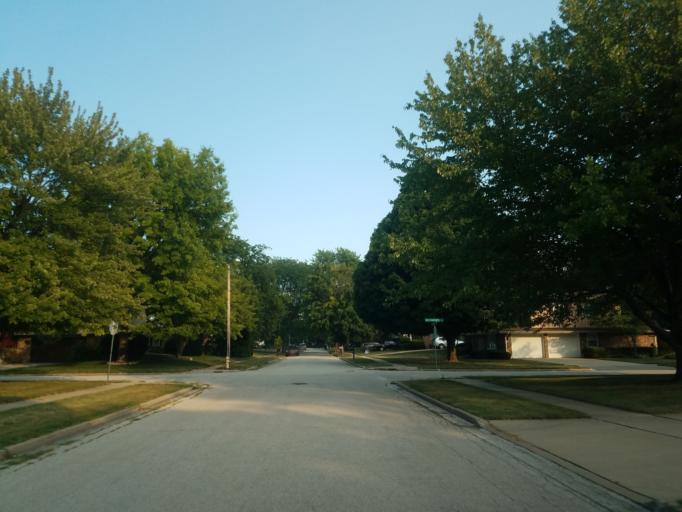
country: US
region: Illinois
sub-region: McLean County
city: Bloomington
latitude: 40.4702
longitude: -88.9458
